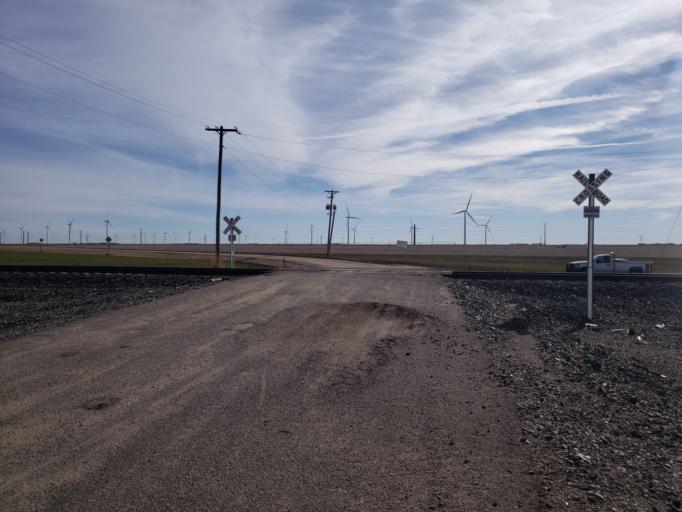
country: US
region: Kansas
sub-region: Ford County
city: Dodge City
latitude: 37.8263
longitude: -99.8063
